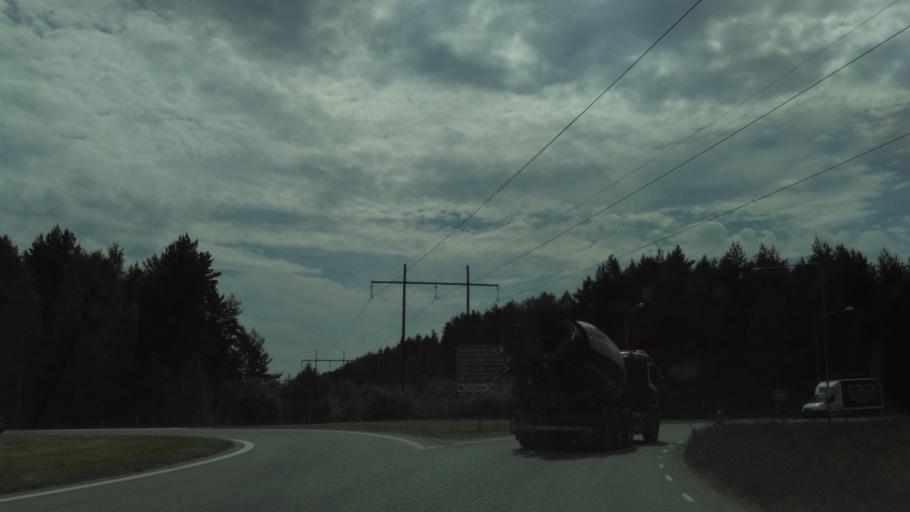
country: SE
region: Vaestra Goetaland
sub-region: Lidkopings Kommun
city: Lidkoping
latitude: 58.4891
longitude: 13.1855
